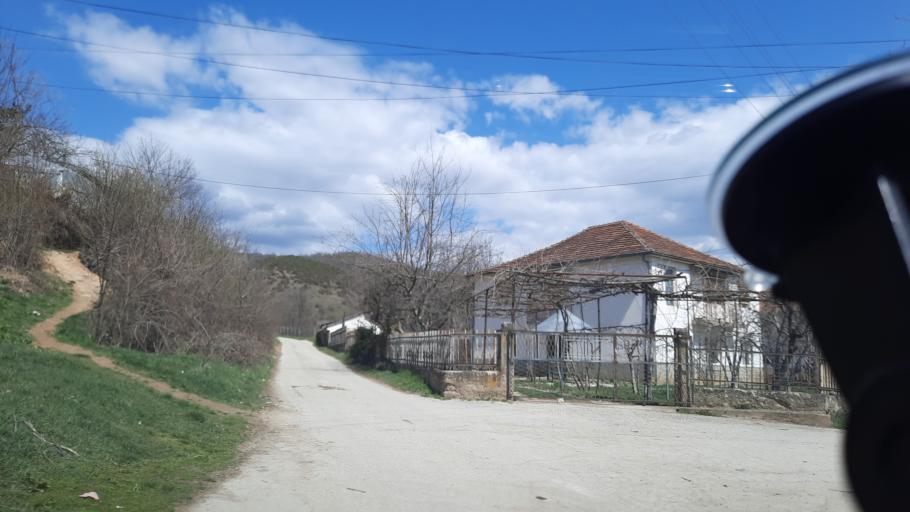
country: MK
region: Demir Hisar
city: Sopotnica
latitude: 41.2944
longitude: 21.1512
